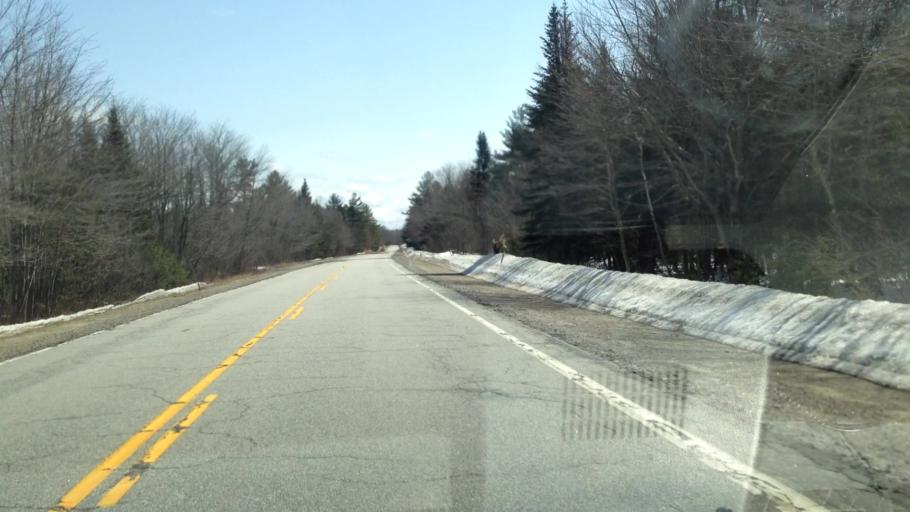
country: US
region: New Hampshire
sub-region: Sullivan County
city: Springfield
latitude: 43.4936
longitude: -71.9922
